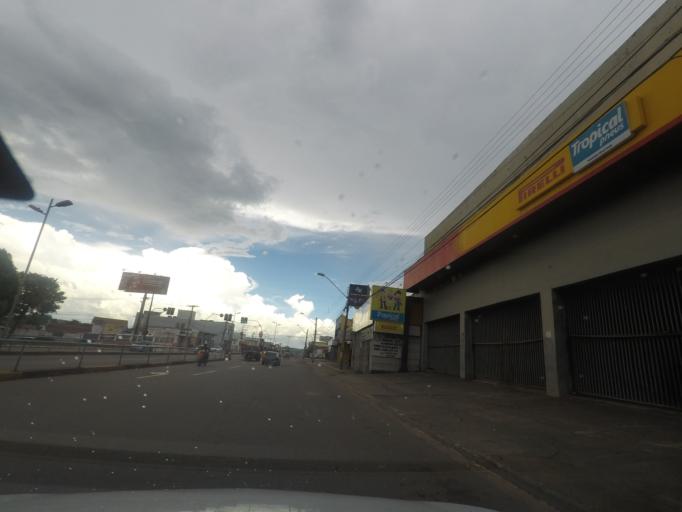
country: BR
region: Goias
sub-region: Goiania
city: Goiania
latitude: -16.6714
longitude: -49.2333
